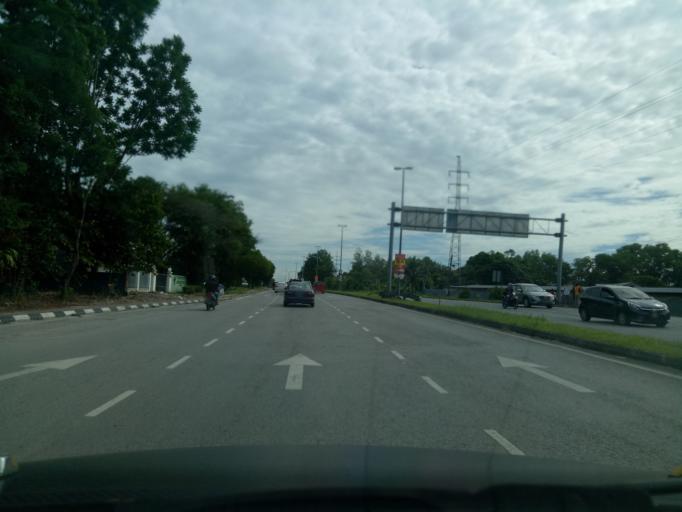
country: MY
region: Sarawak
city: Kuching
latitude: 1.4852
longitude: 110.3312
